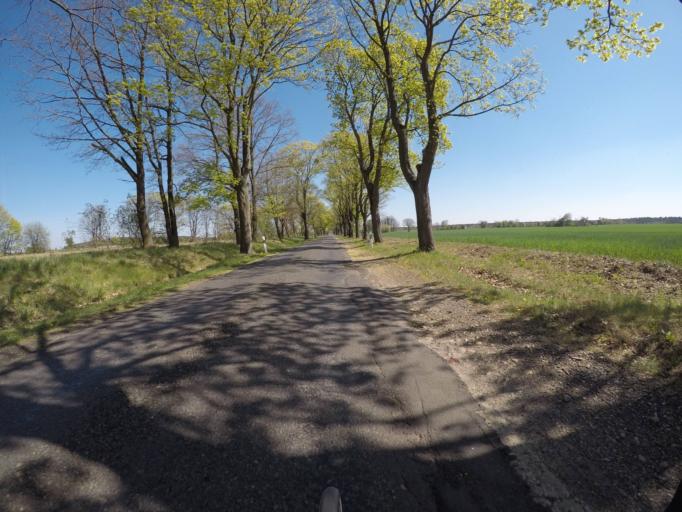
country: DE
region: Brandenburg
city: Strausberg
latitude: 52.6166
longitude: 13.8498
